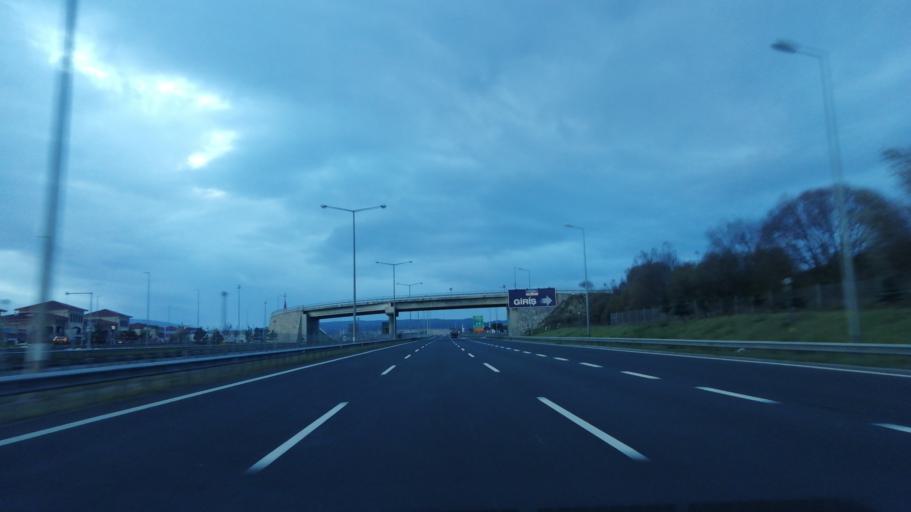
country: TR
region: Bolu
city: Bolu
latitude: 40.7231
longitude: 31.4705
